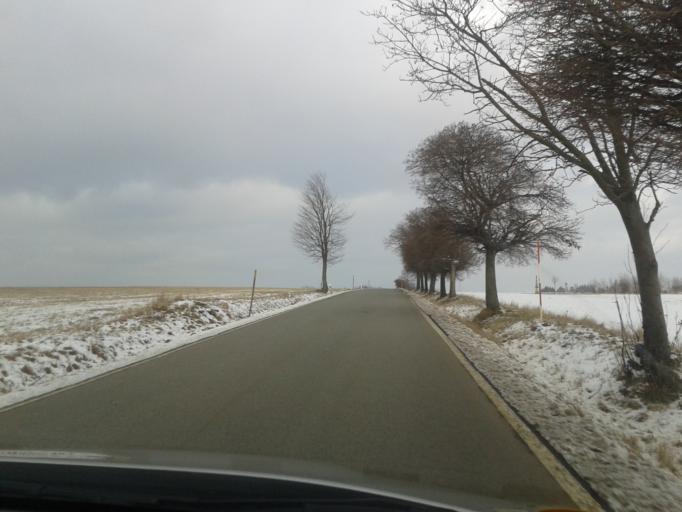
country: CZ
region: Olomoucky
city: Horni Stepanov
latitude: 49.5721
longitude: 16.8229
